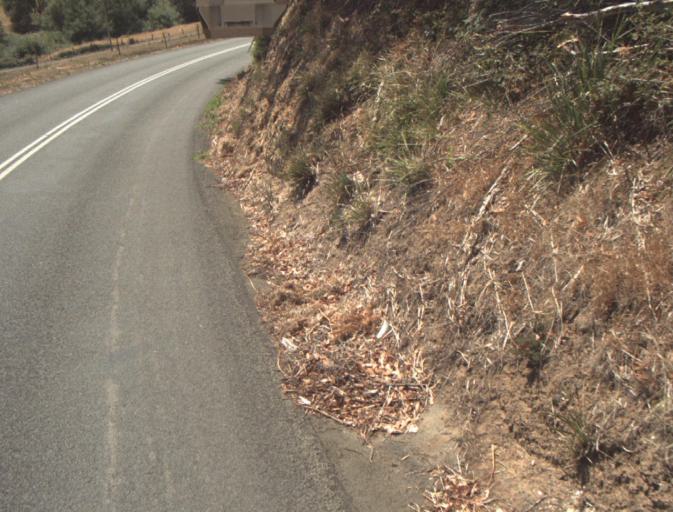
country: AU
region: Tasmania
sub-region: Launceston
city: Mayfield
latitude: -41.2673
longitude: 147.1287
